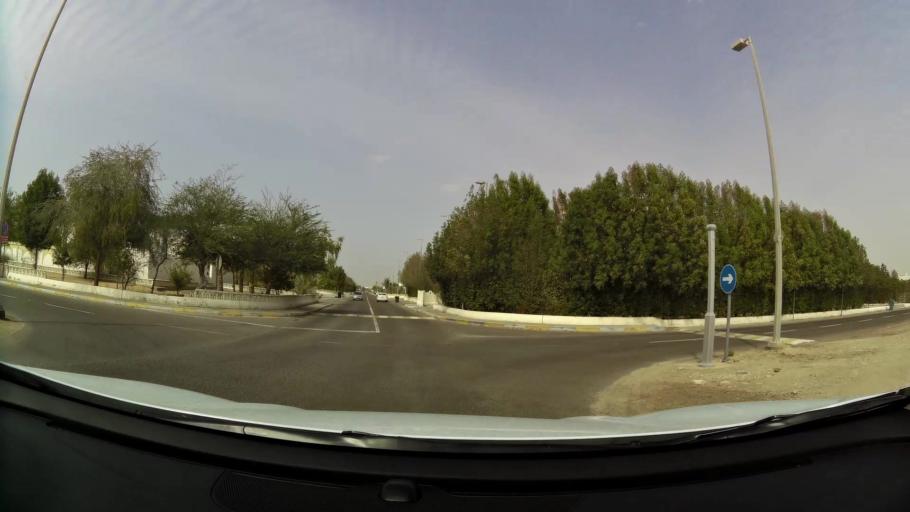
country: AE
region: Abu Dhabi
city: Abu Dhabi
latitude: 24.5652
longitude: 54.6903
